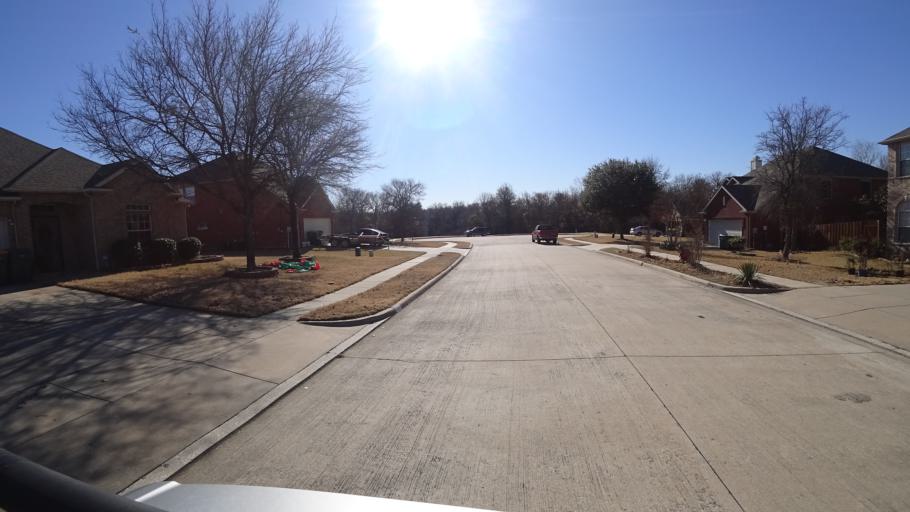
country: US
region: Texas
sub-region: Denton County
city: Lewisville
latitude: 33.0240
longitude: -97.0226
